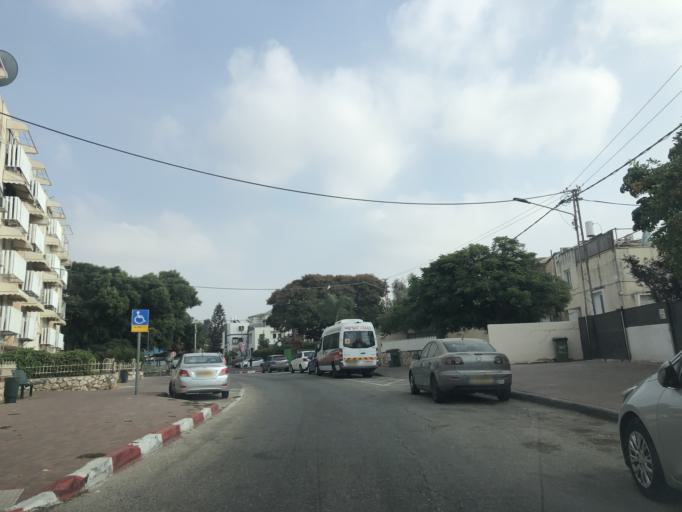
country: IL
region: Central District
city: Rosh Ha'Ayin
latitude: 32.0949
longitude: 34.9516
